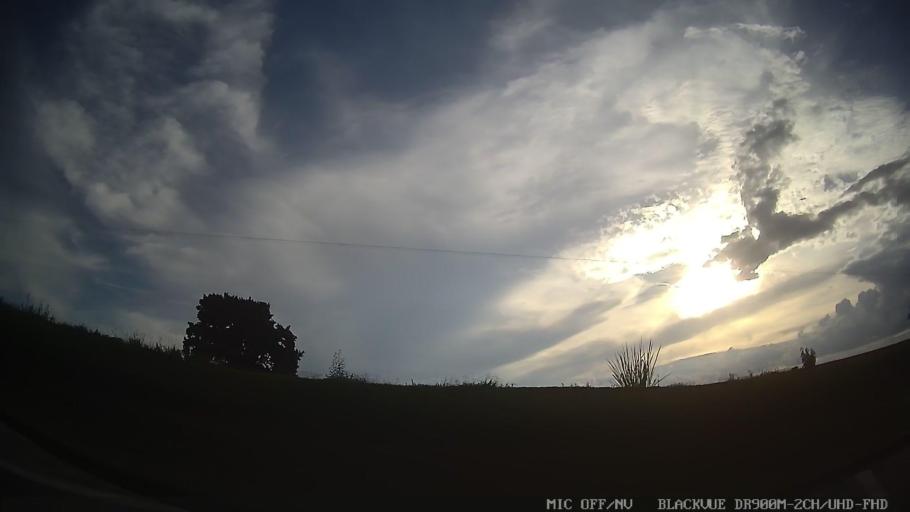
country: BR
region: Sao Paulo
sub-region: Tiete
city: Tiete
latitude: -23.1314
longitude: -47.6938
